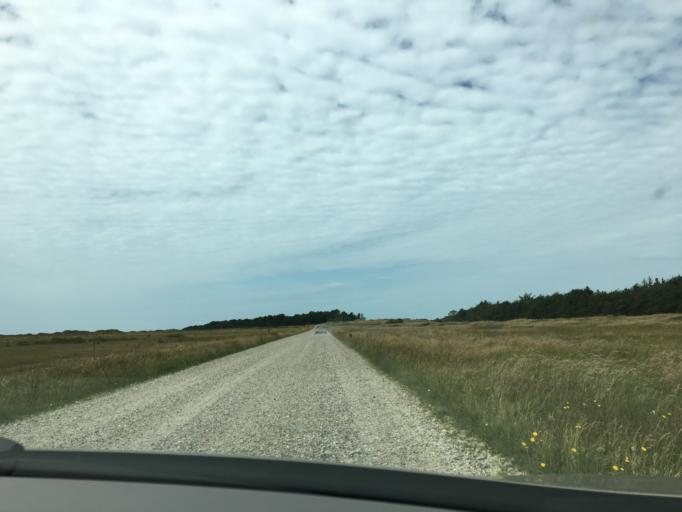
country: DK
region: South Denmark
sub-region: Varde Kommune
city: Oksbol
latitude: 55.7227
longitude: 8.2068
